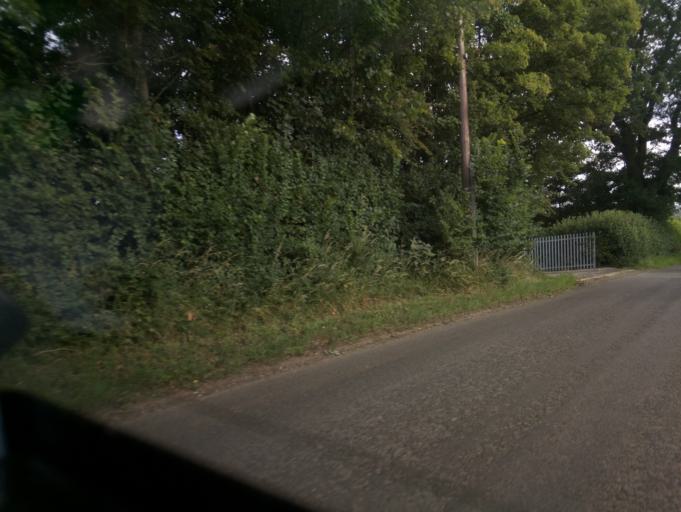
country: GB
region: England
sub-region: Borough of Swindon
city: Hannington
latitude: 51.6169
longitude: -1.7470
